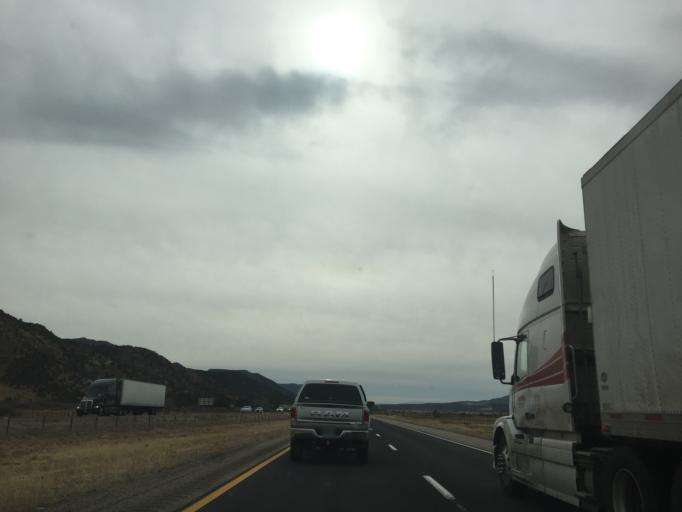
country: US
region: Utah
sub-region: Iron County
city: Cedar City
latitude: 37.4984
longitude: -113.2164
